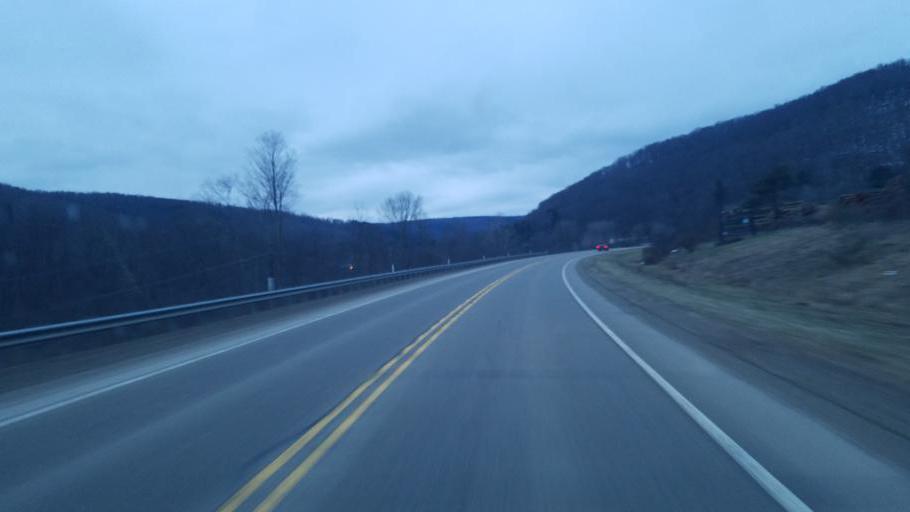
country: US
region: Pennsylvania
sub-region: Potter County
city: Coudersport
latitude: 41.7953
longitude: -78.0155
